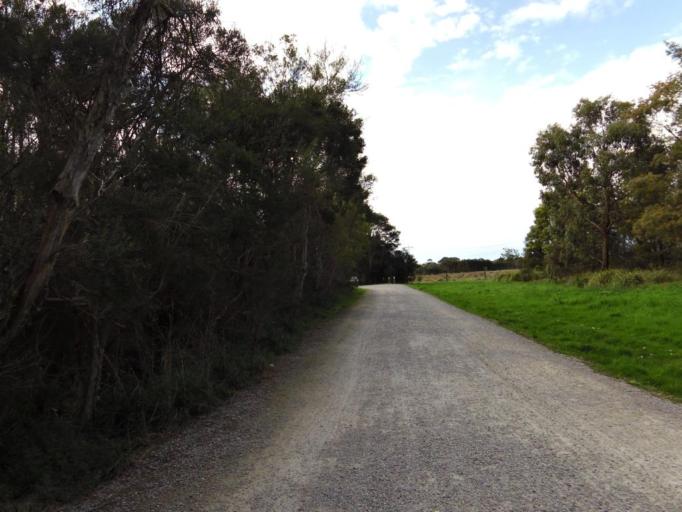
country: AU
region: Victoria
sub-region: Knox
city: Wantirna South
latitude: -37.8952
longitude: 145.2026
